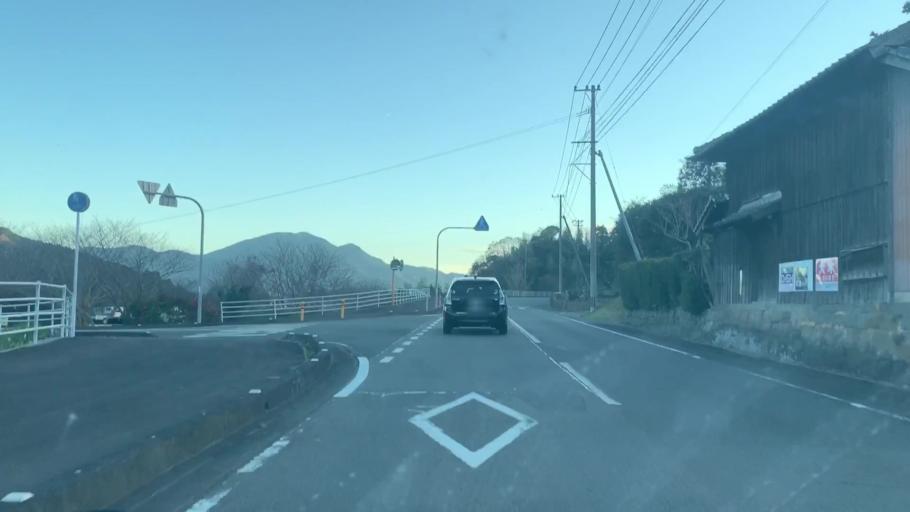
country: JP
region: Saga Prefecture
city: Imaricho-ko
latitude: 33.3235
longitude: 129.9697
